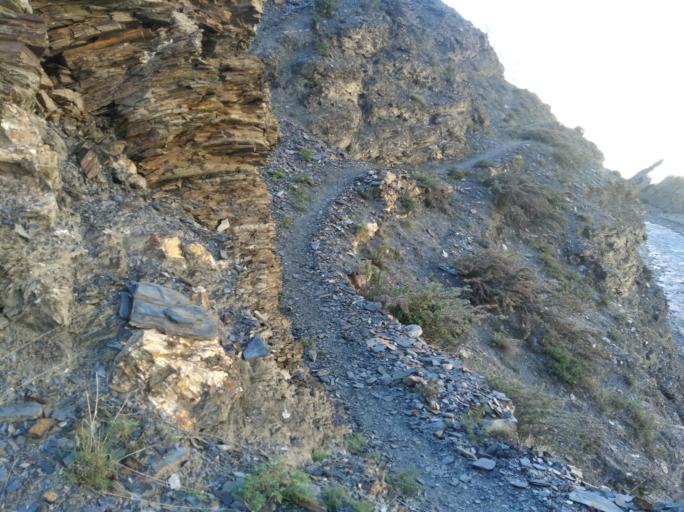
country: NP
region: Western Region
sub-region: Dhawalagiri Zone
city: Jomsom
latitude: 28.8666
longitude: 83.3484
